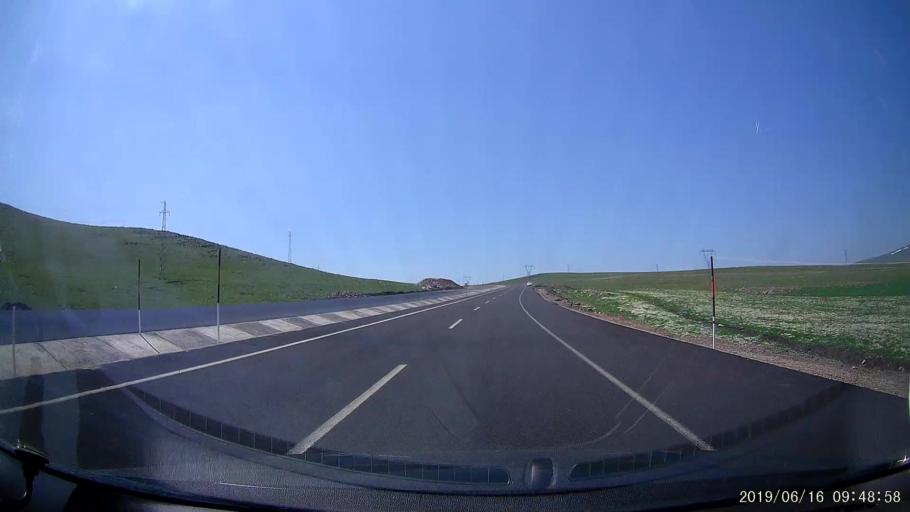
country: TR
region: Kars
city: Digor
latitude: 40.4272
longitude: 43.3561
